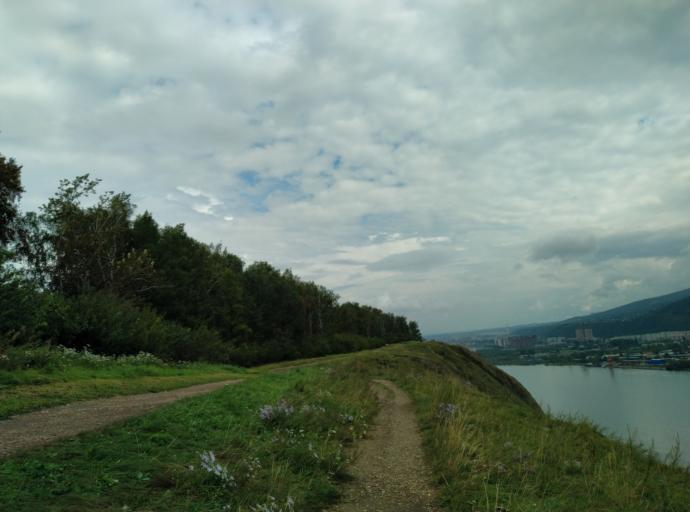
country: RU
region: Krasnoyarskiy
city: Krasnoyarsk
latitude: 55.9829
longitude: 92.7550
